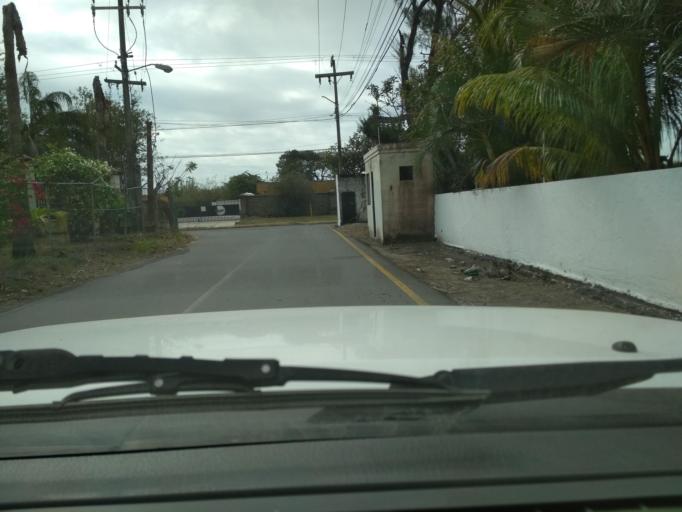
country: MX
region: Veracruz
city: Boca del Rio
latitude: 19.0897
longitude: -96.1171
